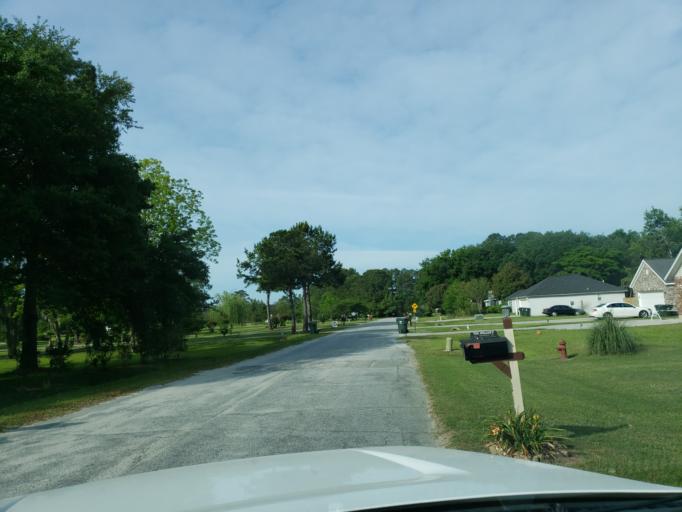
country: US
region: Georgia
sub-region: Chatham County
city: Georgetown
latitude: 32.0040
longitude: -81.2260
